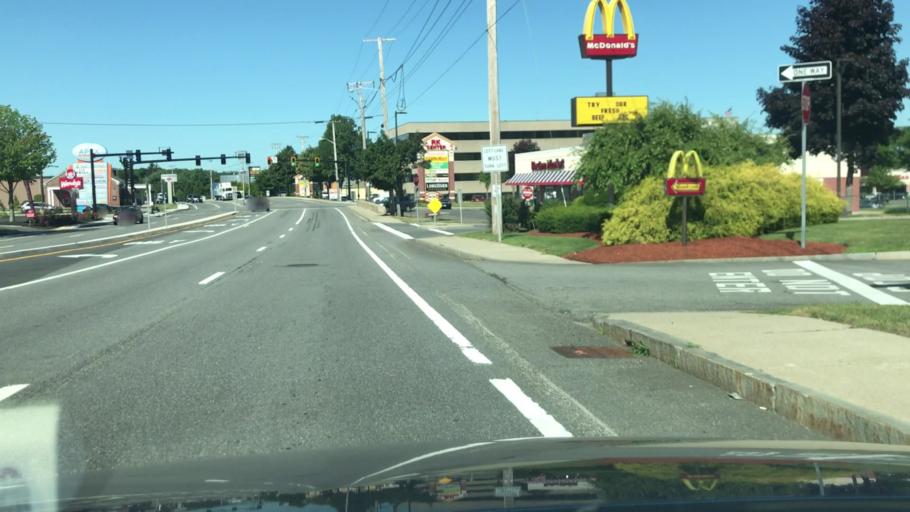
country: US
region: Massachusetts
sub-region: Middlesex County
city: Marlborough
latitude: 42.3393
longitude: -71.5884
